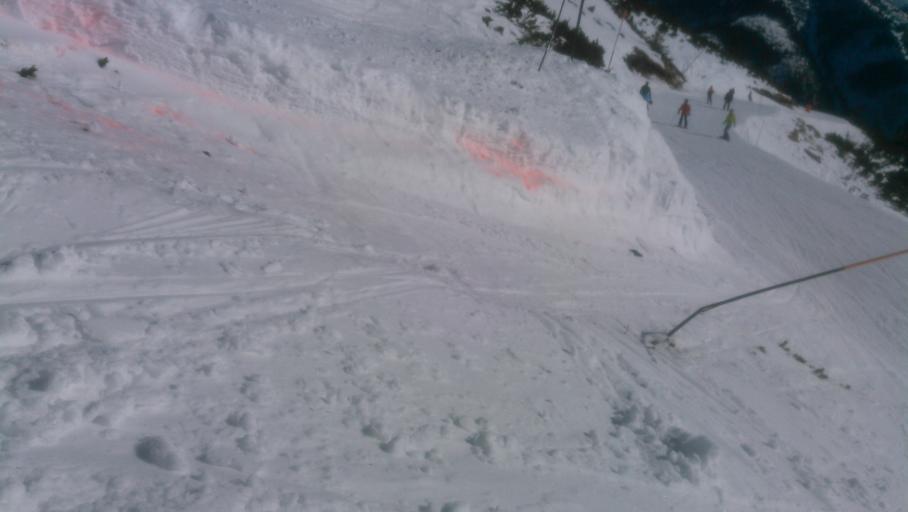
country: SK
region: Banskobystricky
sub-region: Okres Banska Bystrica
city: Brezno
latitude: 48.9352
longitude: 19.5881
